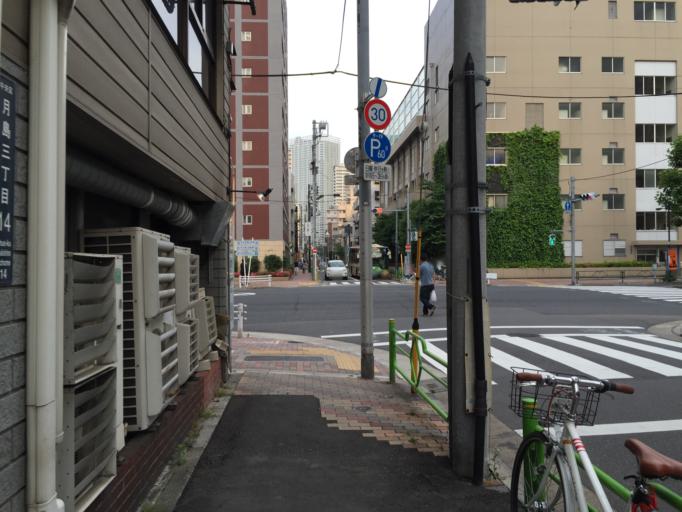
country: JP
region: Tokyo
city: Tokyo
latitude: 35.6615
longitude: 139.7802
